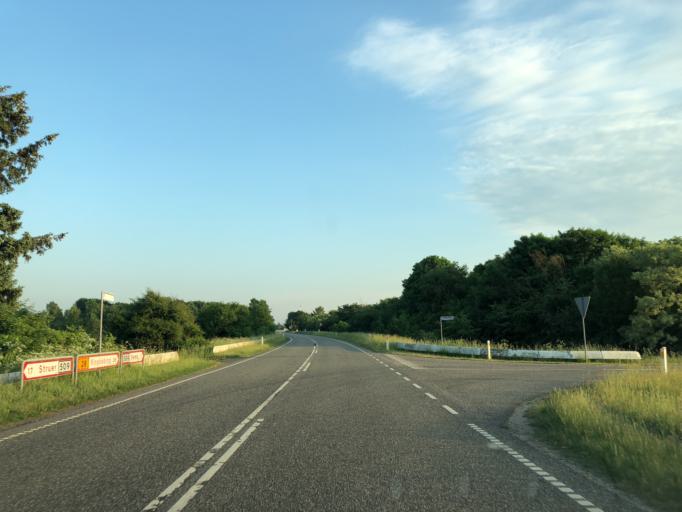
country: DK
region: Central Jutland
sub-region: Holstebro Kommune
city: Ulfborg
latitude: 56.3716
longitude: 8.4410
